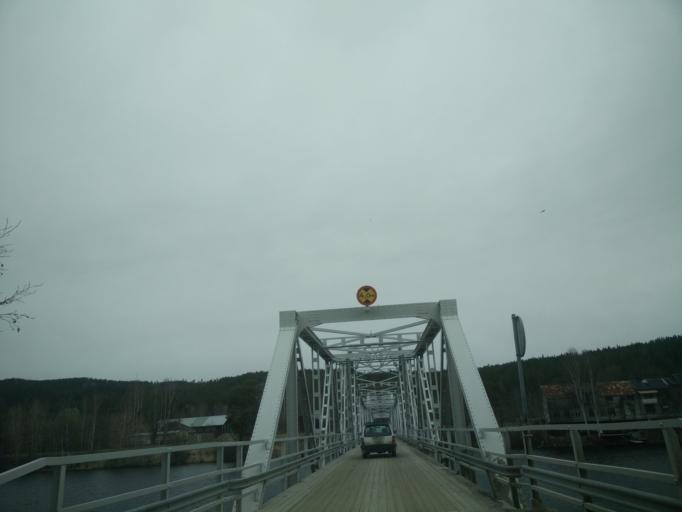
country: SE
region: Vaesternorrland
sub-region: Ange Kommun
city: Fransta
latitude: 62.4477
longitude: 16.4325
